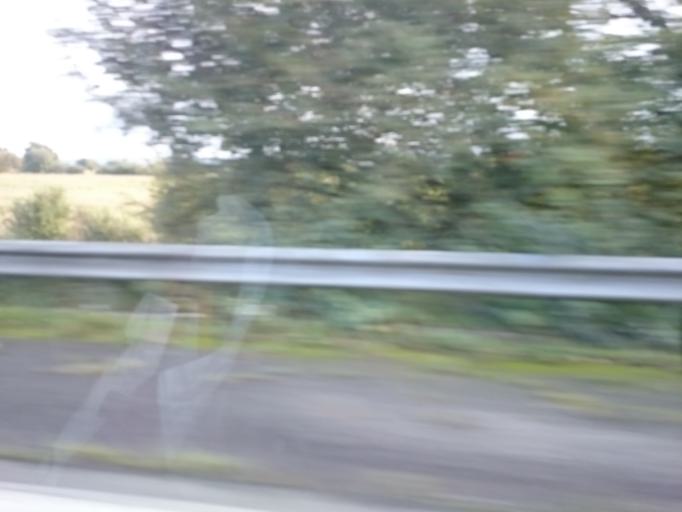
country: FR
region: Brittany
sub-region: Departement des Cotes-d'Armor
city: Louargat
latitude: 48.5664
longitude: -3.3212
